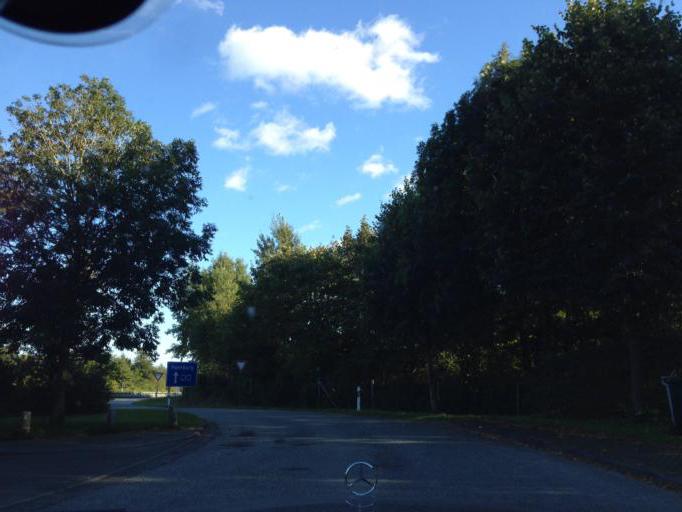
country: DE
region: Schleswig-Holstein
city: Schackendorf
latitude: 53.9591
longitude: 10.2614
